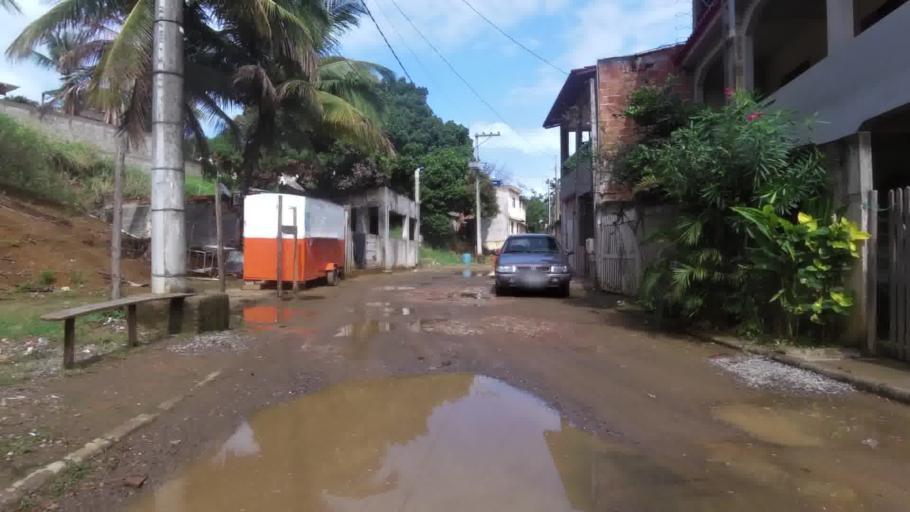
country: BR
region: Espirito Santo
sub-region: Piuma
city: Piuma
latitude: -20.8311
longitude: -40.7006
